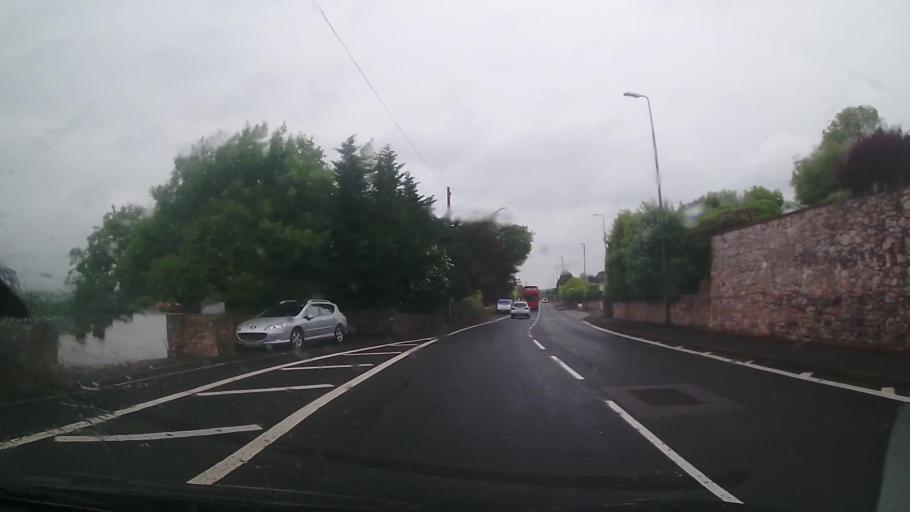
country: GB
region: England
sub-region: Borough of Torbay
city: Paignton
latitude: 50.4081
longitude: -3.5630
